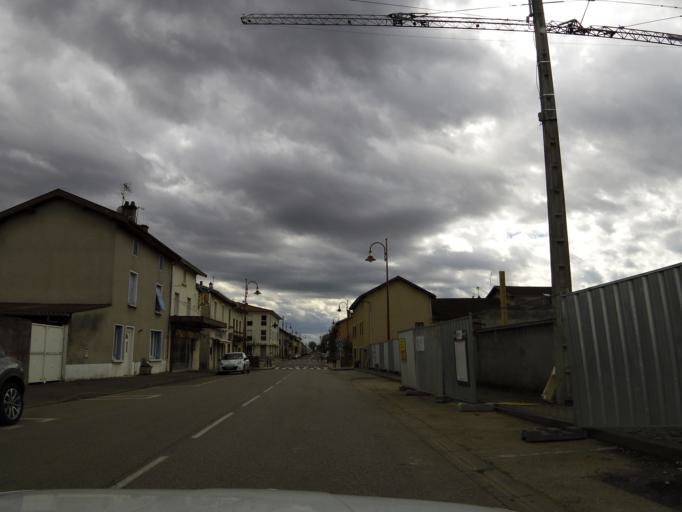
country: FR
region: Rhone-Alpes
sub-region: Departement de l'Ain
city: Meximieux
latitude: 45.9214
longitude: 5.2241
